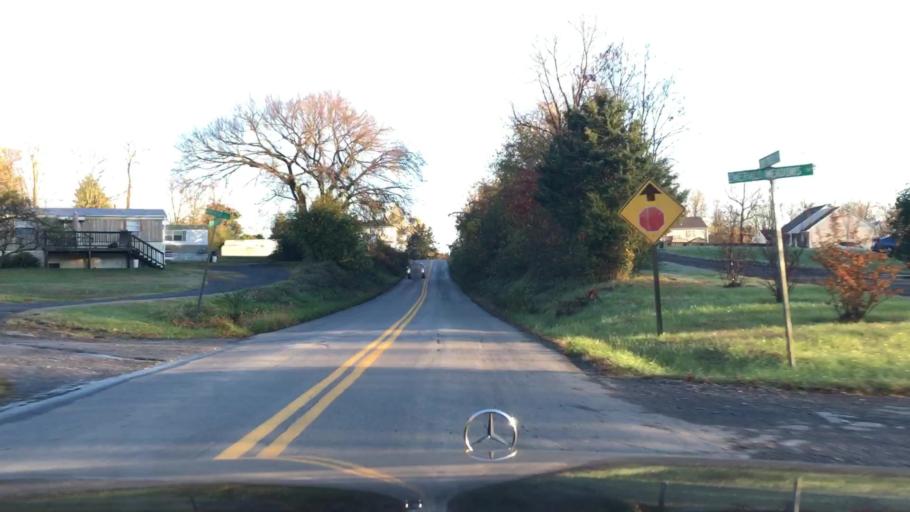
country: US
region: Virginia
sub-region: Campbell County
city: Timberlake
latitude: 37.3001
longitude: -79.2813
